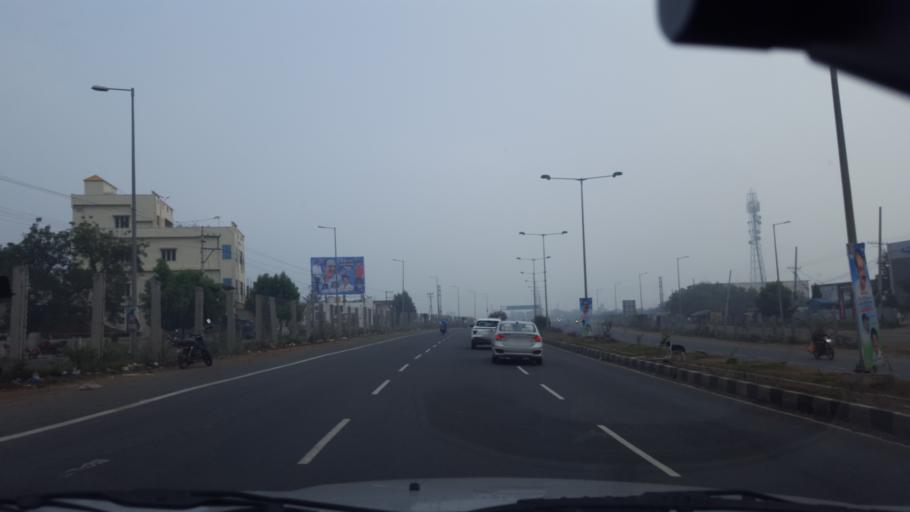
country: IN
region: Andhra Pradesh
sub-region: Prakasam
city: Ongole
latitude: 15.5448
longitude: 80.0527
